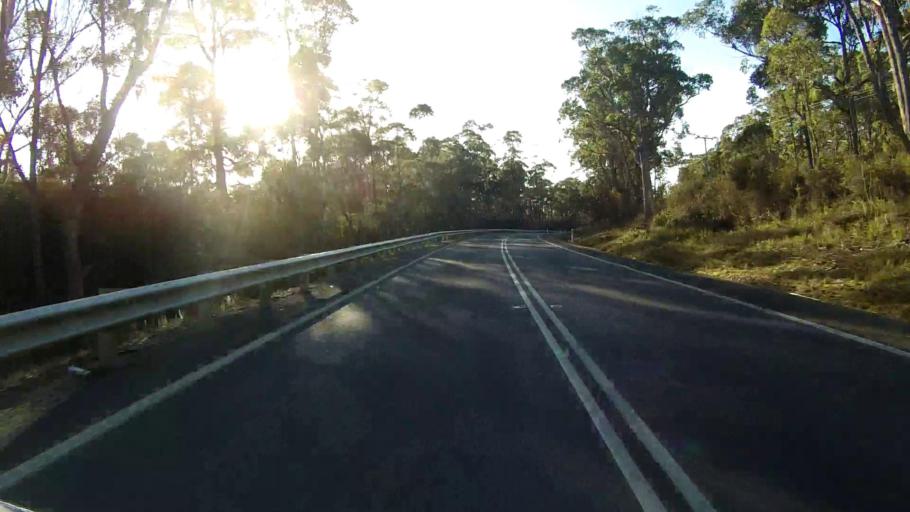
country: AU
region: Tasmania
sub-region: Clarence
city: Sandford
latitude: -43.0786
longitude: 147.8627
